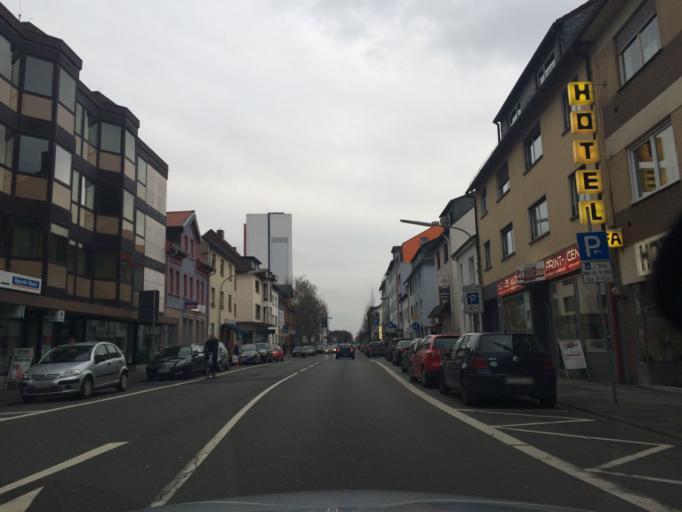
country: DE
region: Hesse
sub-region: Regierungsbezirk Darmstadt
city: Neu Isenburg
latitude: 50.0513
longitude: 8.6952
